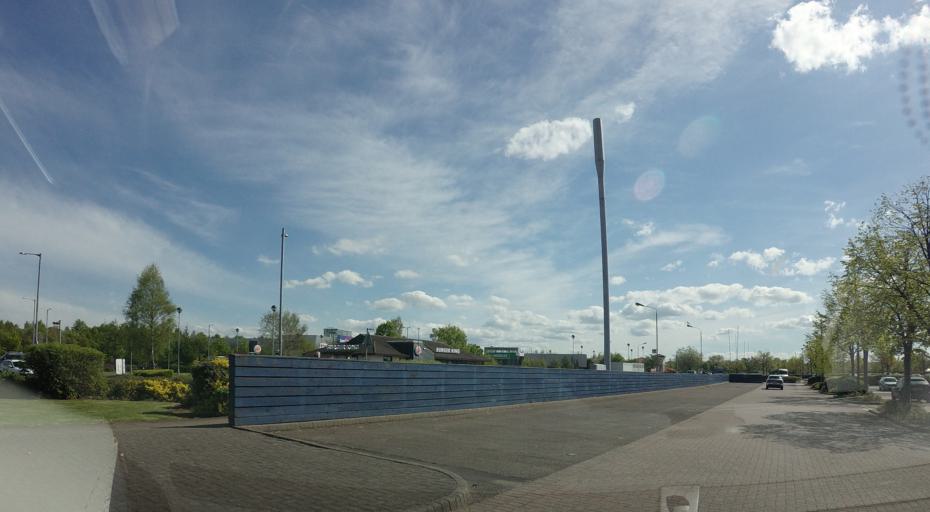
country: GB
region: Scotland
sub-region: Stirling
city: Bannockburn
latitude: 56.1150
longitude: -3.9093
